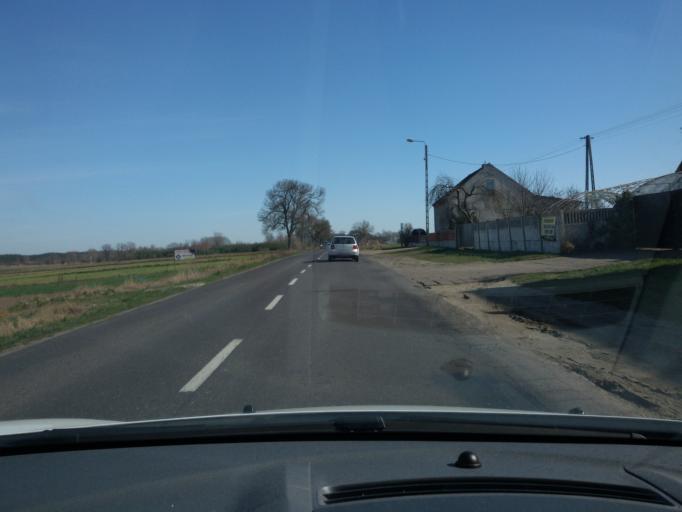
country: PL
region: Greater Poland Voivodeship
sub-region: Powiat gostynski
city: Poniec
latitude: 51.7580
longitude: 16.8271
